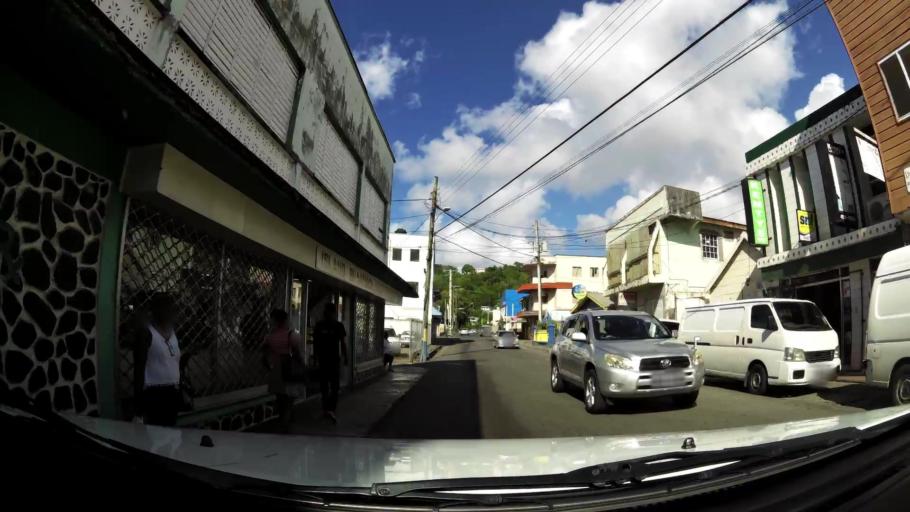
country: LC
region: Castries Quarter
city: Bisee
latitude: 14.0102
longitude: -60.9868
